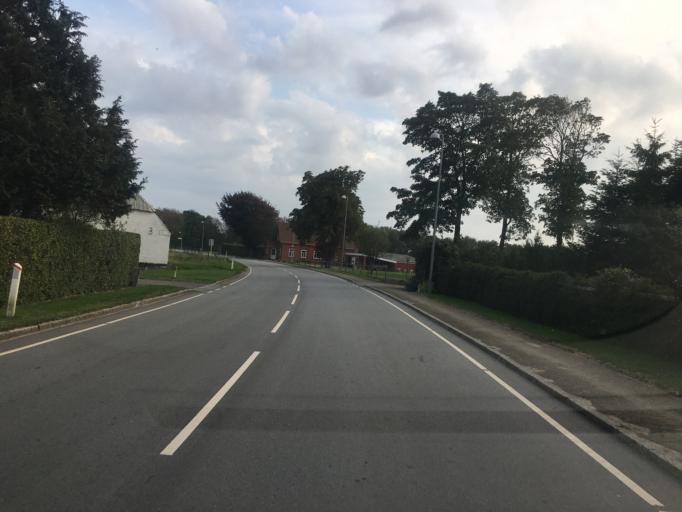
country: DE
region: Schleswig-Holstein
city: Bramstedtlund
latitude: 54.9166
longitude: 9.0708
